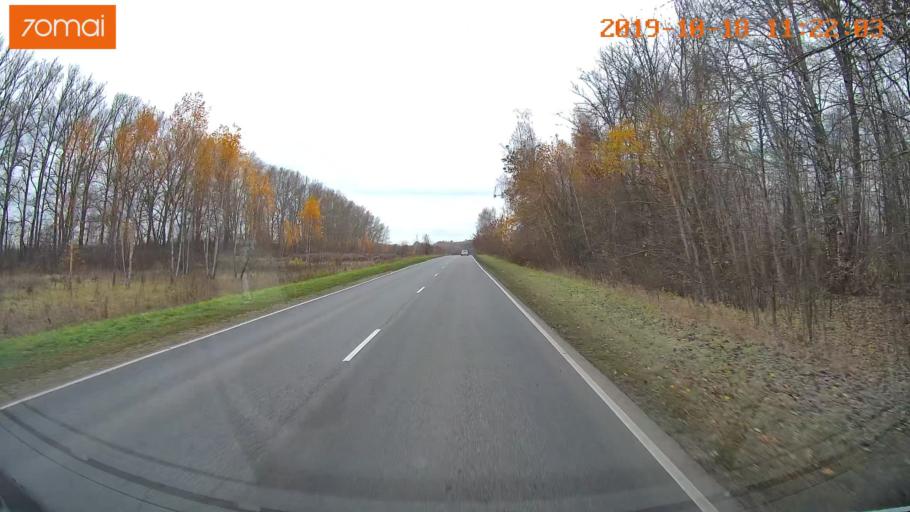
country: RU
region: Tula
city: Kimovsk
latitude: 54.0822
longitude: 38.5748
